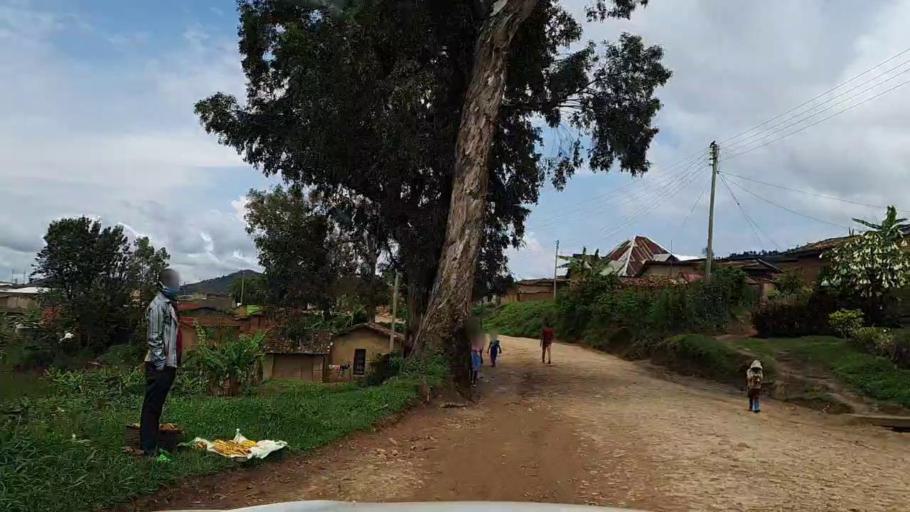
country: RW
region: Southern Province
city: Gikongoro
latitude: -2.3303
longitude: 29.5297
